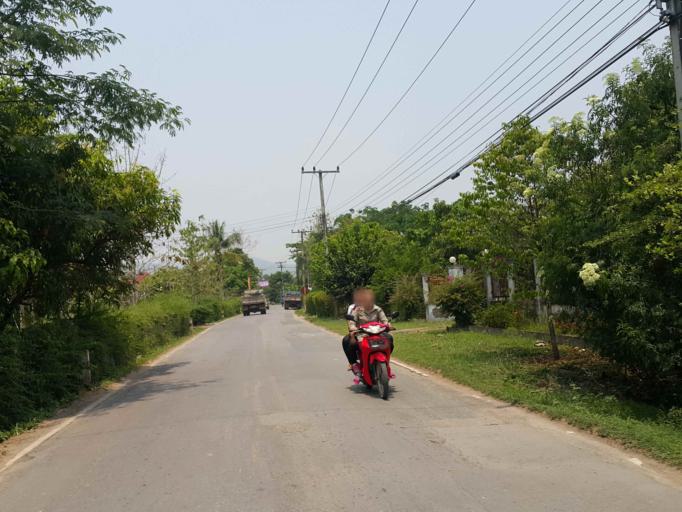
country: TH
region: Chiang Mai
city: San Sai
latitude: 18.8946
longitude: 99.0834
